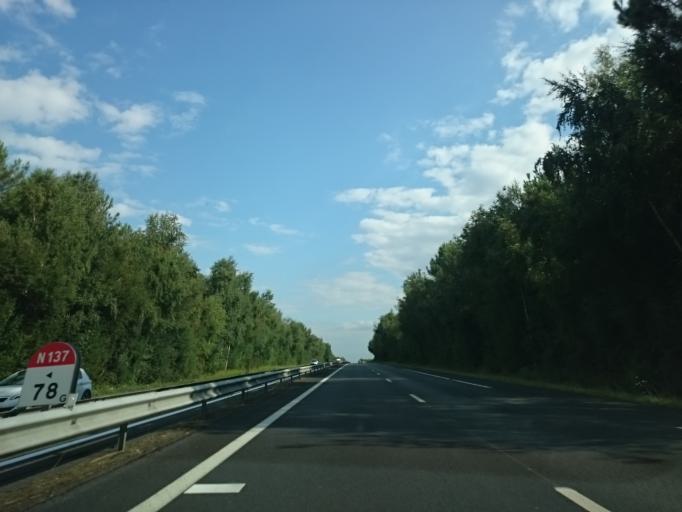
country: FR
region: Pays de la Loire
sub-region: Departement de la Loire-Atlantique
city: Derval
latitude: 47.6776
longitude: -1.6926
